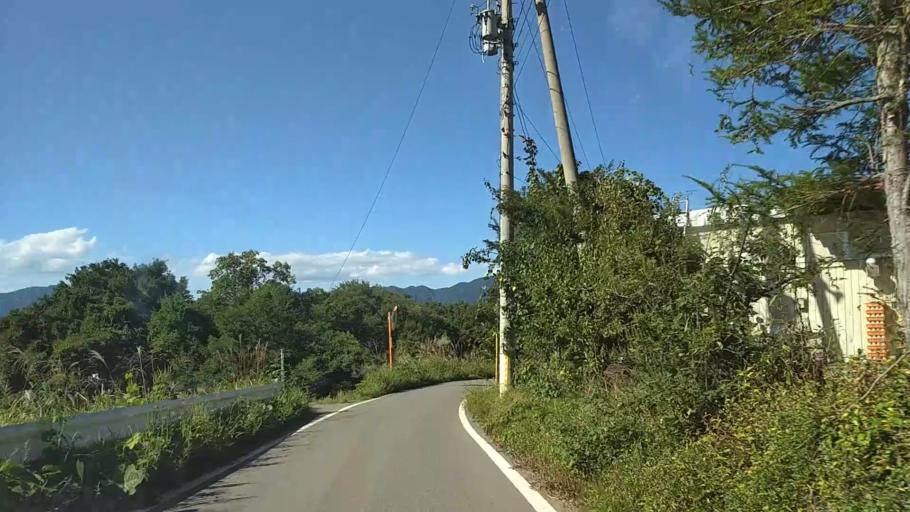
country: JP
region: Nagano
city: Nagano-shi
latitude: 36.5858
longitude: 138.0885
